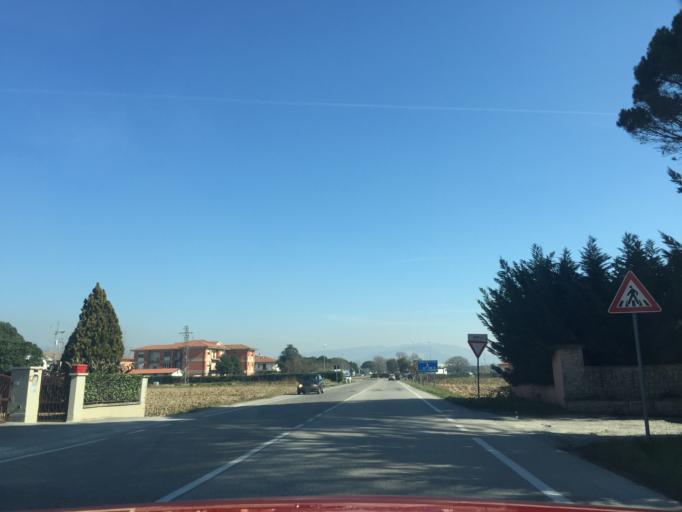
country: IT
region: Tuscany
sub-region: Provincia di Pistoia
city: Ponte Buggianese
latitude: 43.8522
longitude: 10.7442
